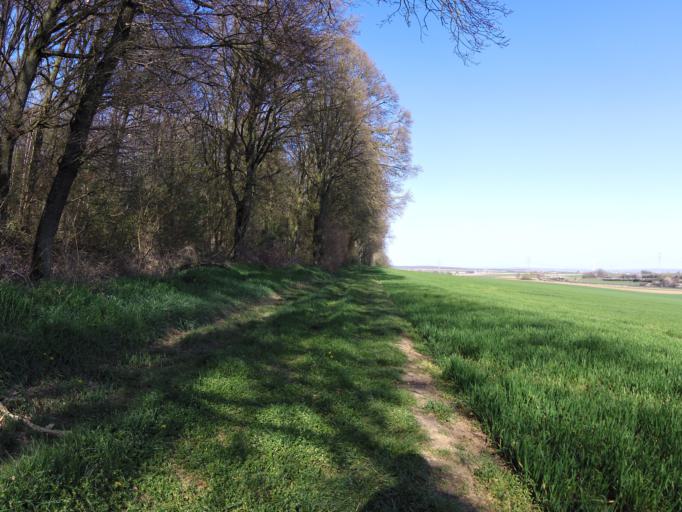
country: DE
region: Bavaria
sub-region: Regierungsbezirk Unterfranken
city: Kurnach
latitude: 49.8255
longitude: 10.0670
